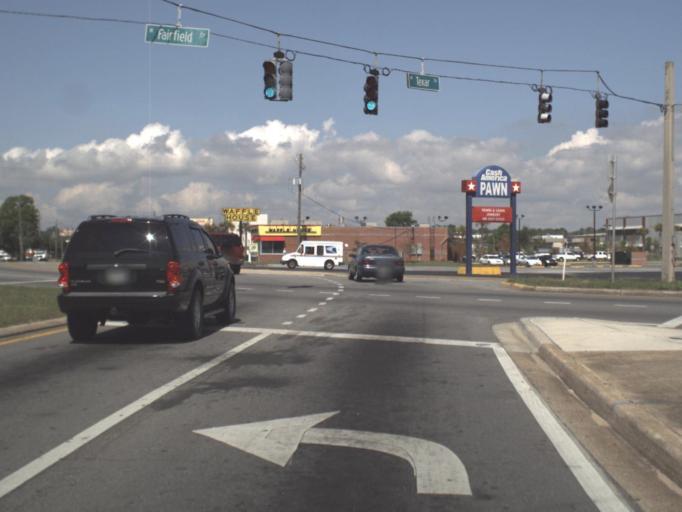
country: US
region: Florida
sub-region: Escambia County
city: Goulding
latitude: 30.4451
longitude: -87.2316
